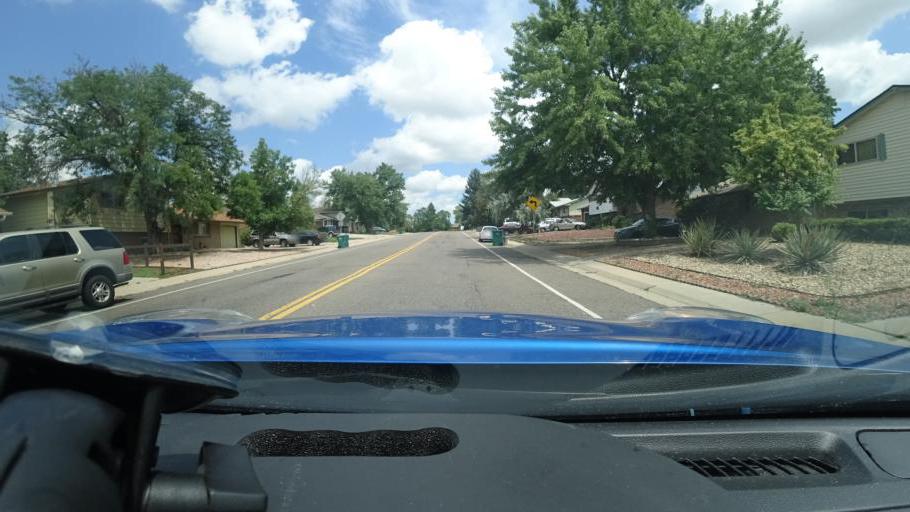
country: US
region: Colorado
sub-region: Adams County
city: Aurora
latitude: 39.6981
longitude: -104.8323
